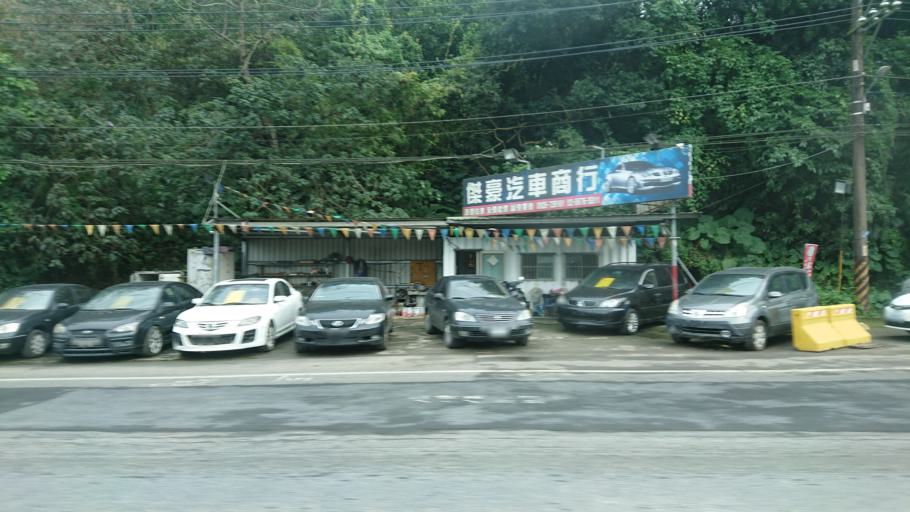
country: TW
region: Taipei
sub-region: Taipei
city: Banqiao
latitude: 24.9479
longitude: 121.4066
